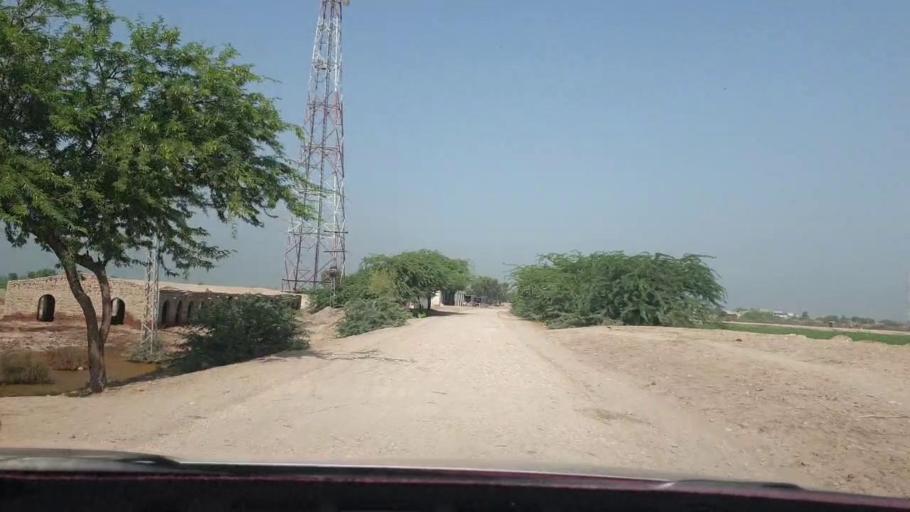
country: PK
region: Sindh
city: Nasirabad
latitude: 27.4193
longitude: 67.9303
